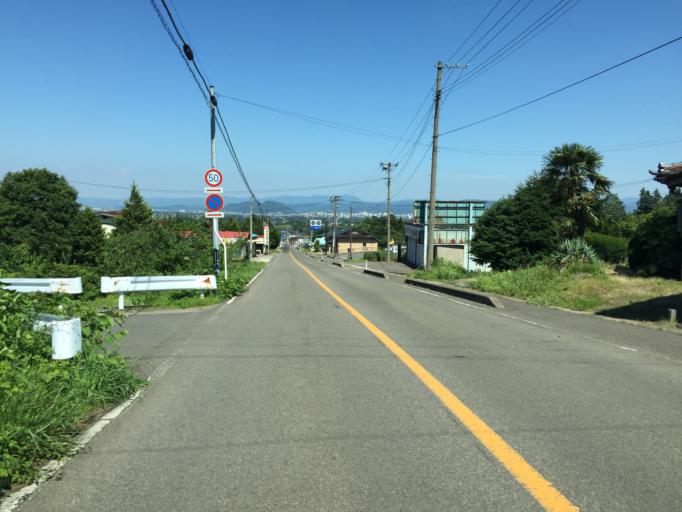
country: JP
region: Fukushima
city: Fukushima-shi
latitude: 37.7550
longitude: 140.3569
